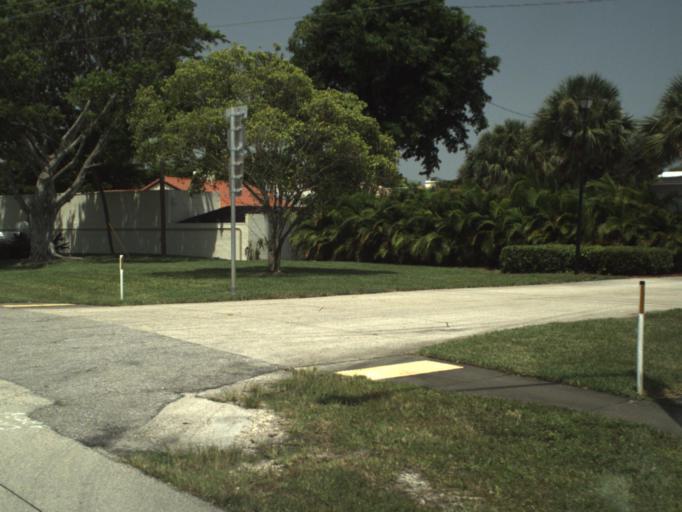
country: US
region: Florida
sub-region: Palm Beach County
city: Boca Del Mar
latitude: 26.3593
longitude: -80.1533
